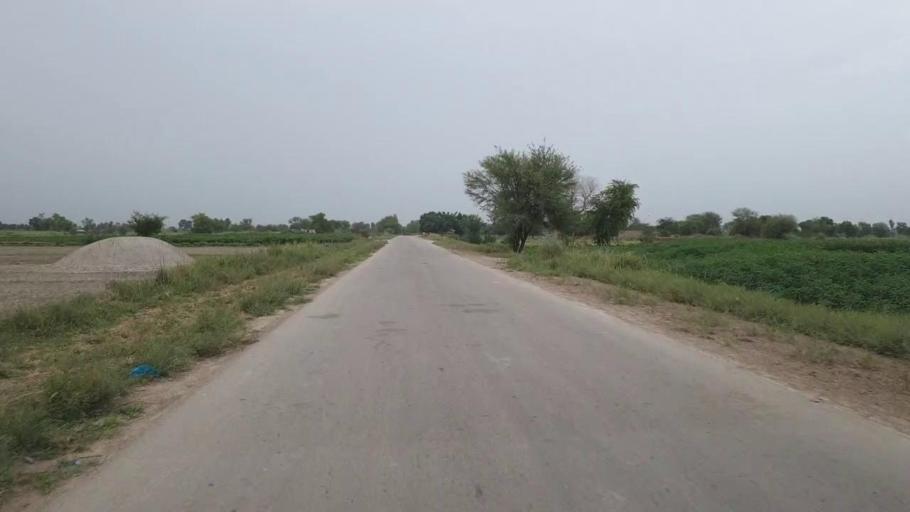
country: PK
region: Sindh
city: Bandhi
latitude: 26.5411
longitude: 68.2194
